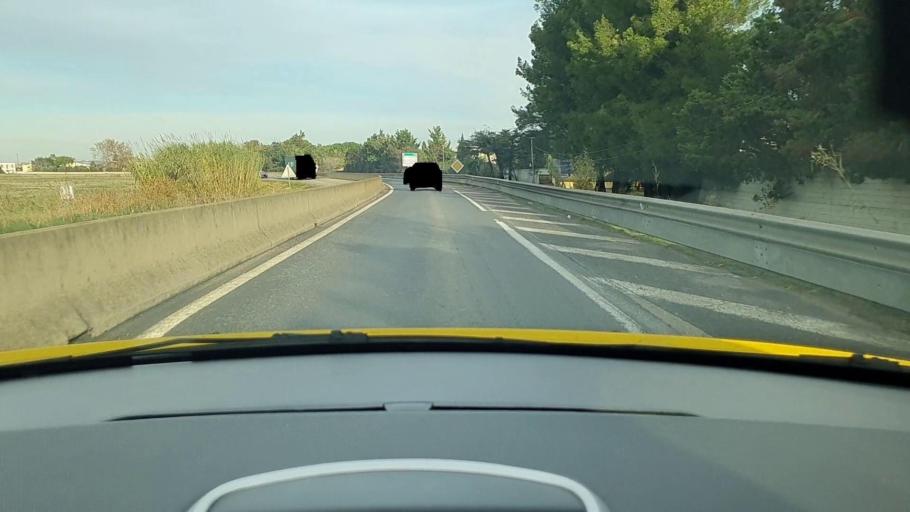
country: FR
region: Languedoc-Roussillon
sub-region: Departement du Gard
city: Fourques
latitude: 43.6915
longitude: 4.6045
